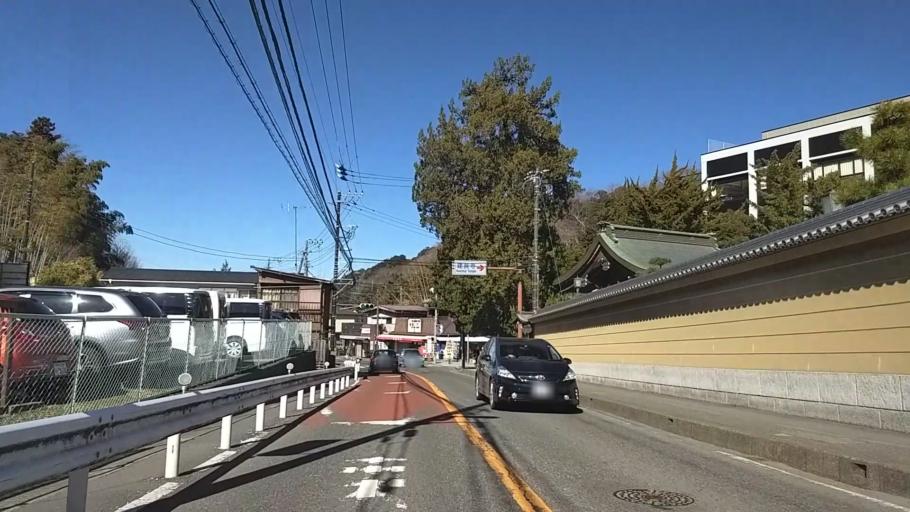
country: JP
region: Kanagawa
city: Kamakura
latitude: 35.3304
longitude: 139.5529
